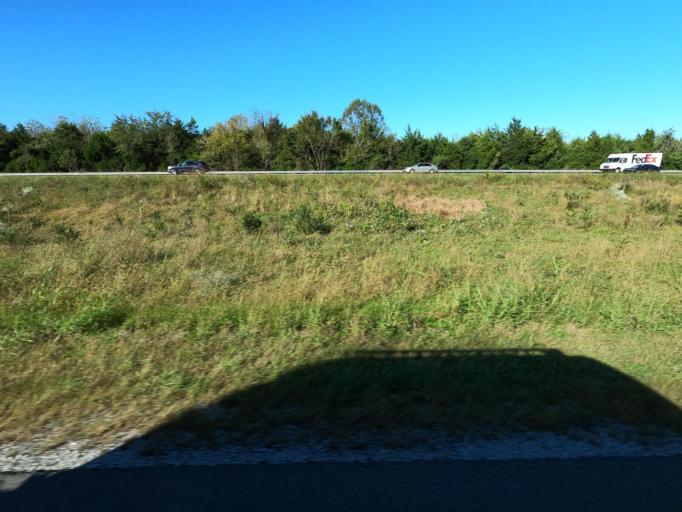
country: US
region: Tennessee
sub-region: Rutherford County
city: Plainview
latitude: 35.5977
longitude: -86.2392
